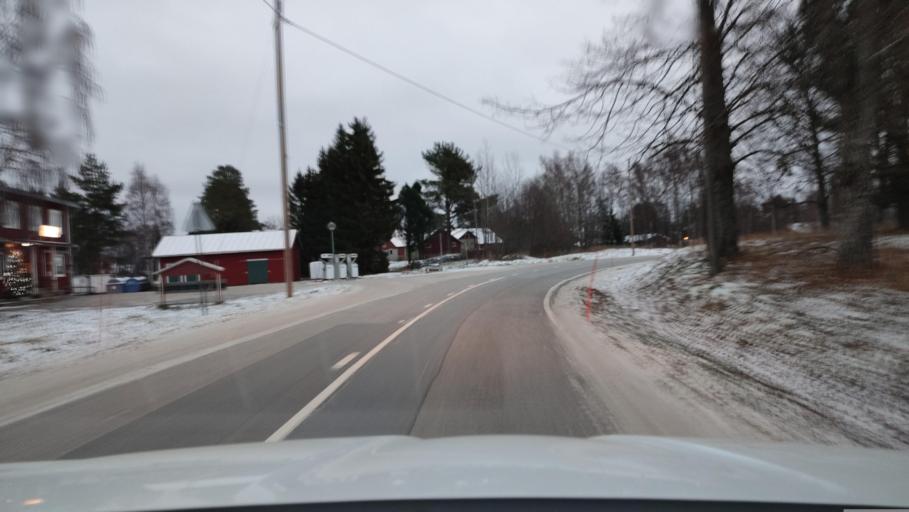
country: FI
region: Ostrobothnia
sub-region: Vaasa
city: Replot
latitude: 63.3451
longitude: 21.3218
